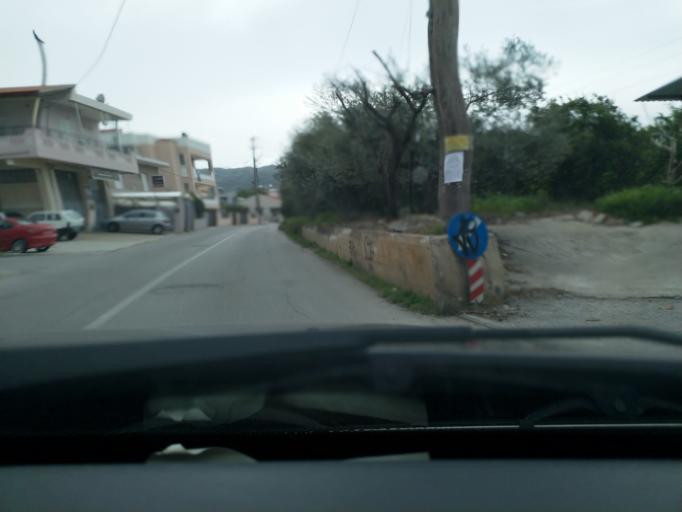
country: GR
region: Crete
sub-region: Nomos Chanias
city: Chania
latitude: 35.4988
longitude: 24.0216
